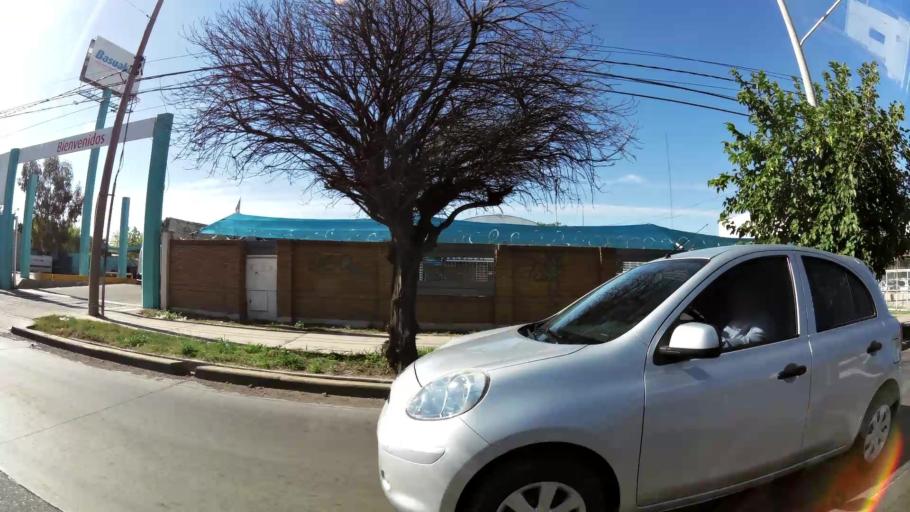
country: AR
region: Mendoza
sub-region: Departamento de Godoy Cruz
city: Godoy Cruz
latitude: -32.9283
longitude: -68.8139
